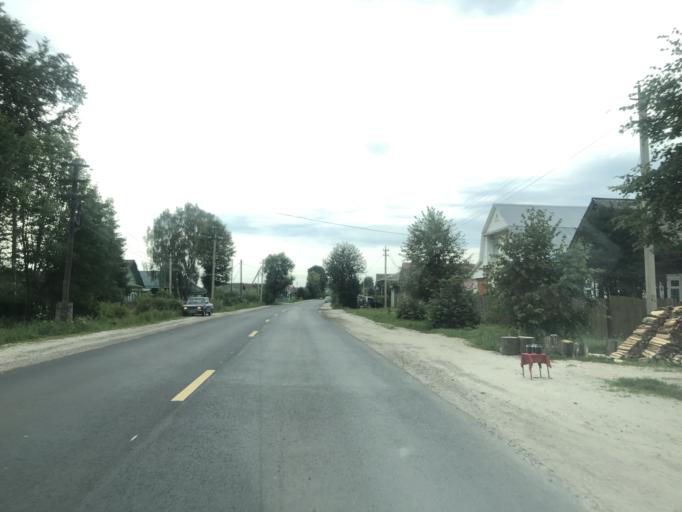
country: RU
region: Ivanovo
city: Pestyaki
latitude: 56.7054
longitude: 42.6820
